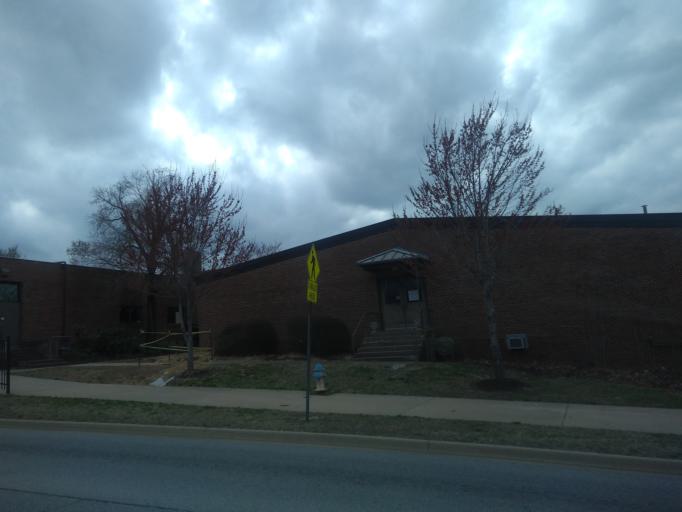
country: US
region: Arkansas
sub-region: Washington County
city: Fayetteville
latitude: 36.0746
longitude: -94.1754
